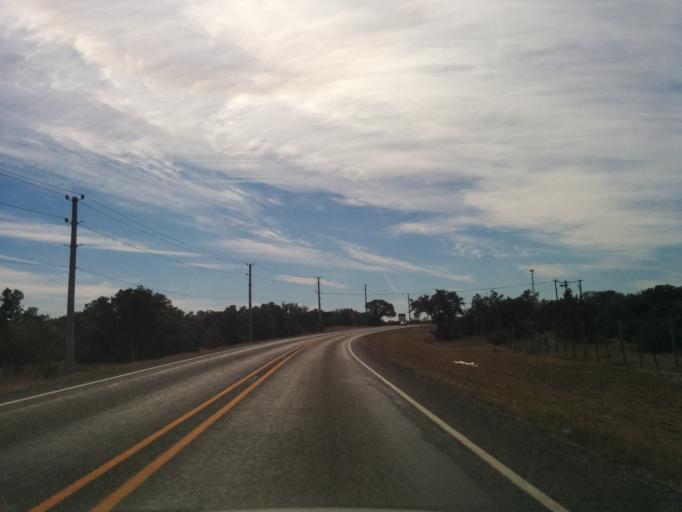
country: US
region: Texas
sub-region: Bexar County
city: Fair Oaks Ranch
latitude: 29.8728
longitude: -98.5586
